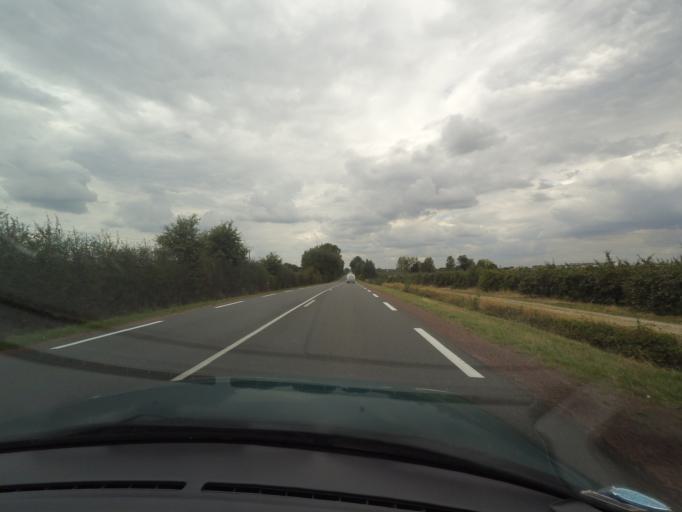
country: FR
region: Poitou-Charentes
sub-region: Departement des Deux-Sevres
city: Viennay
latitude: 46.6894
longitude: -0.2714
